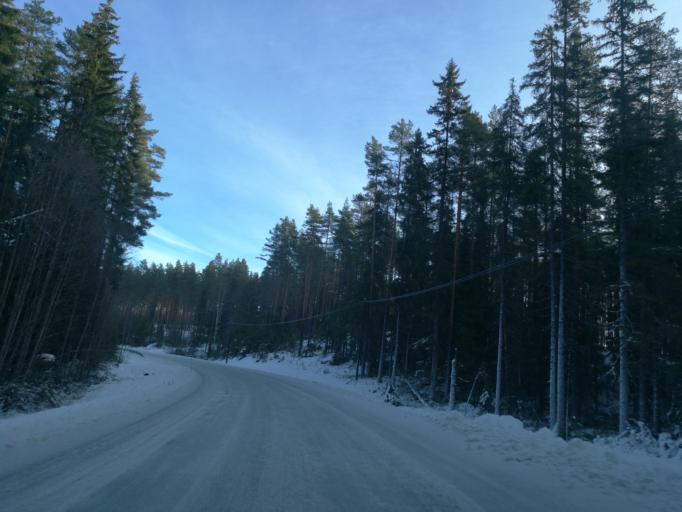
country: NO
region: Hedmark
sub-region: Grue
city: Kirkenaer
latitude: 60.3462
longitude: 12.3184
